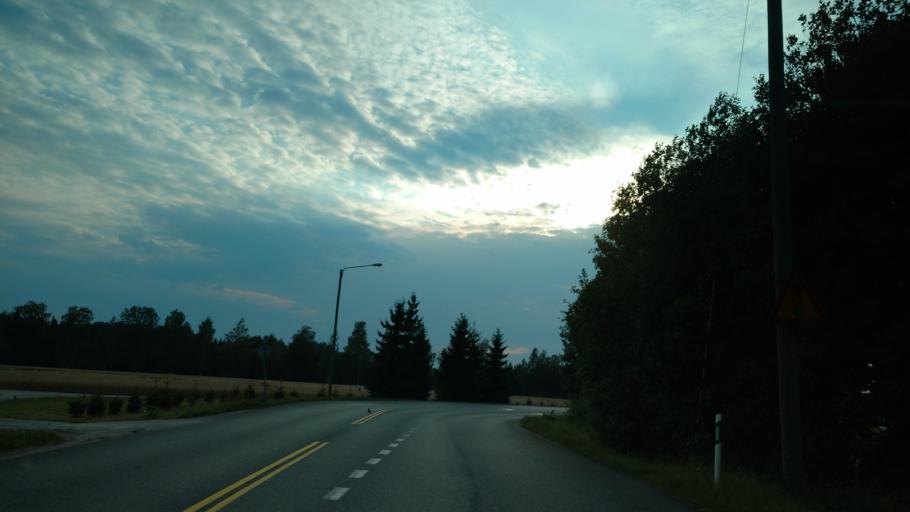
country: FI
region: Varsinais-Suomi
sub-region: Salo
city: Halikko
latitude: 60.3915
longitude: 23.0850
